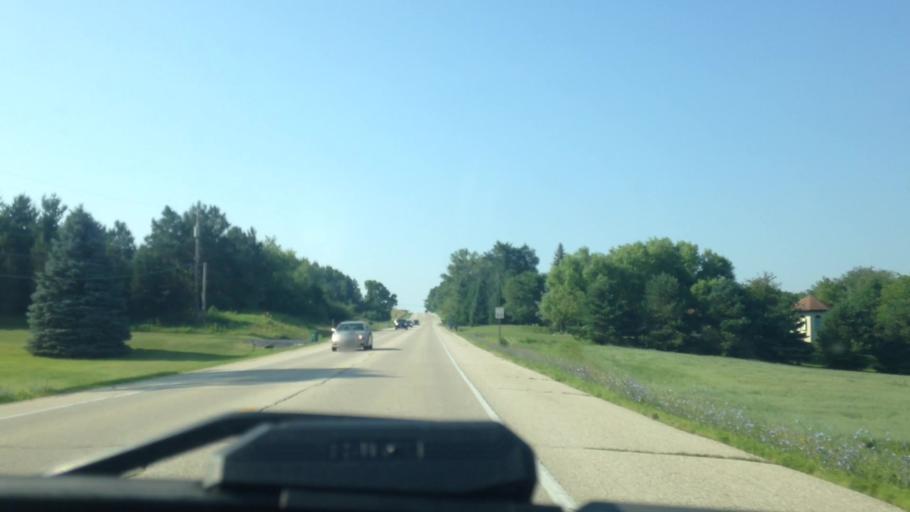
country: US
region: Wisconsin
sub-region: Washington County
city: Richfield
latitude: 43.2407
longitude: -88.2619
